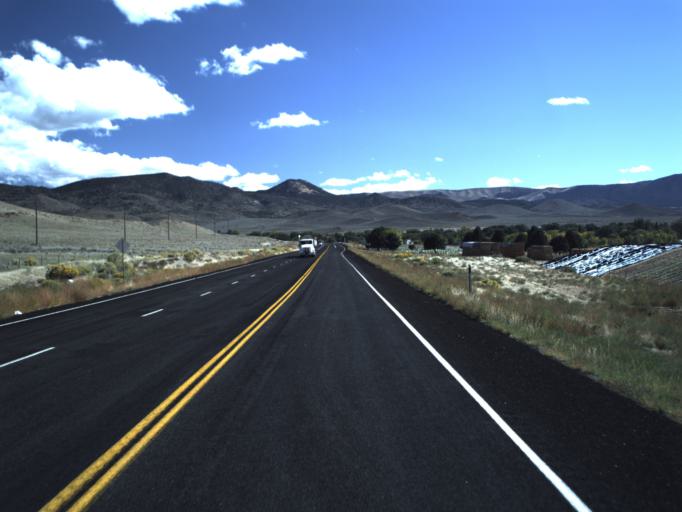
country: US
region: Utah
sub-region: Beaver County
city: Milford
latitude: 38.2286
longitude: -112.9309
